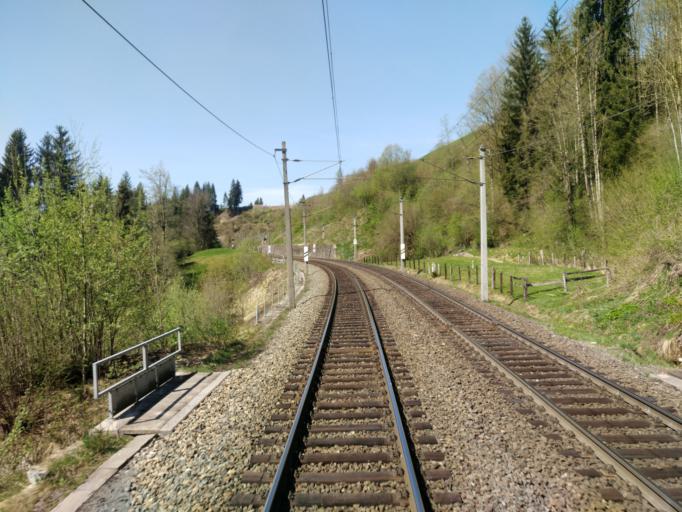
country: AT
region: Tyrol
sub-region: Politischer Bezirk Kitzbuhel
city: Hopfgarten im Brixental
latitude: 47.4337
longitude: 12.1808
